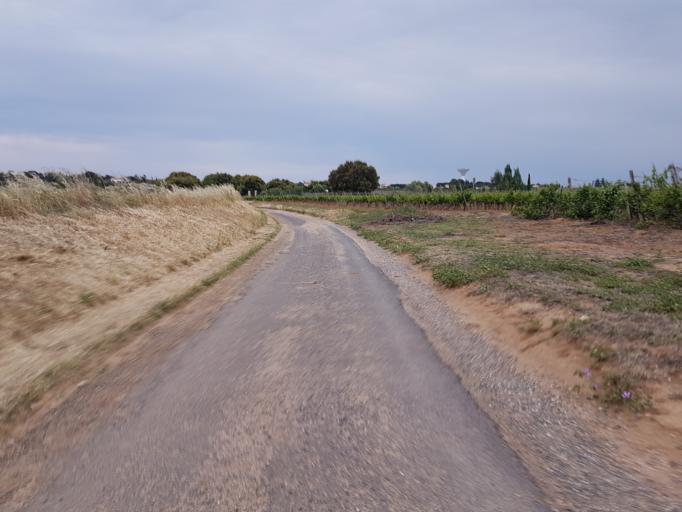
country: FR
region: Languedoc-Roussillon
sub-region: Departement de l'Herault
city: Portiragnes
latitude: 43.3154
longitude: 3.3356
